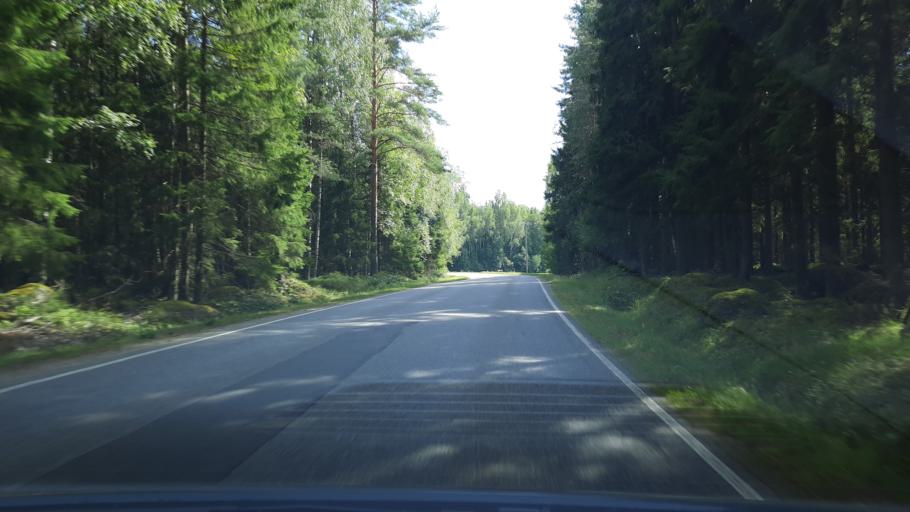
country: FI
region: Pirkanmaa
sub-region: Etelae-Pirkanmaa
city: Urjala
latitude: 61.1767
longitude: 23.3663
